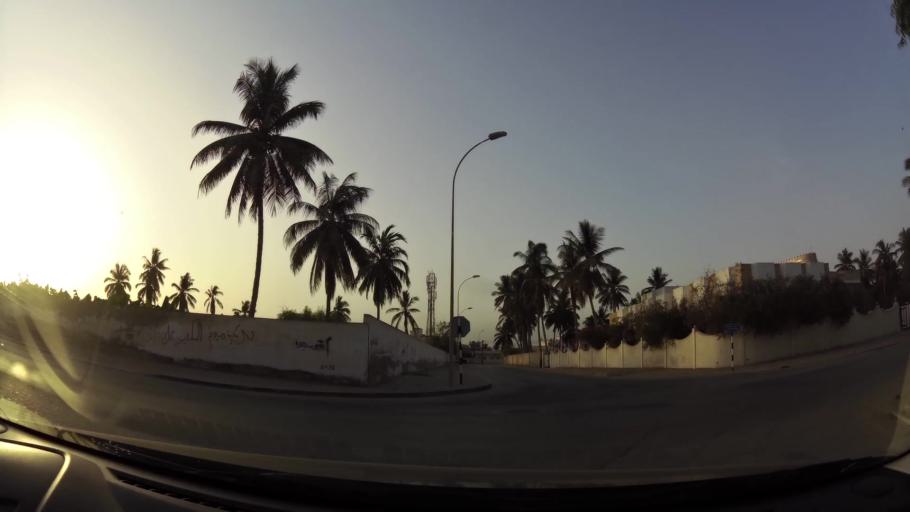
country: OM
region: Zufar
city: Salalah
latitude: 17.0161
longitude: 54.1165
